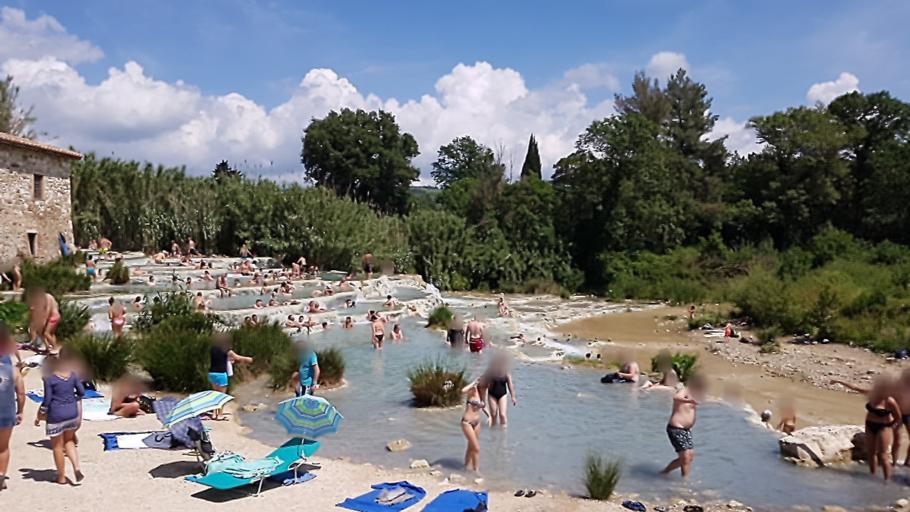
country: IT
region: Tuscany
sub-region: Provincia di Grosseto
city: Manciano
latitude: 42.6481
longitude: 11.5123
